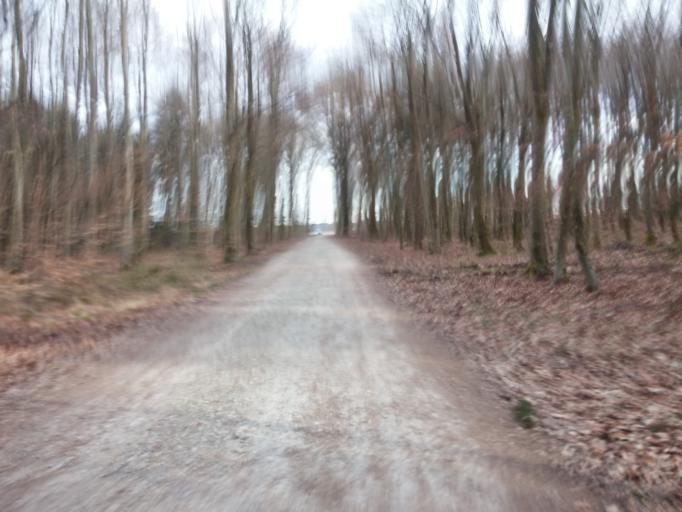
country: DE
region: Bavaria
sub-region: Upper Bavaria
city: Vaterstetten
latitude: 48.0810
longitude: 11.7708
